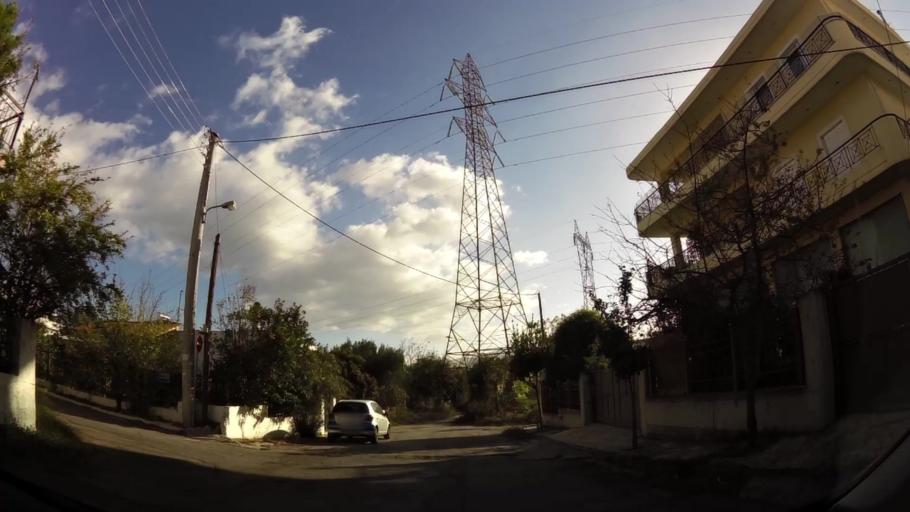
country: GR
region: Attica
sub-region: Nomarchia Anatolikis Attikis
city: Acharnes
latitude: 38.0713
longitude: 23.7460
